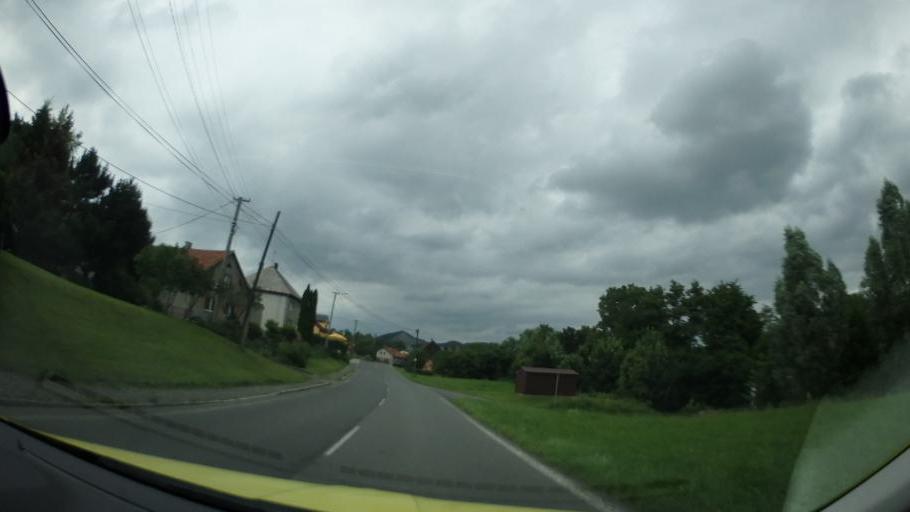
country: CZ
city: Verovice
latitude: 49.5587
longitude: 18.1053
